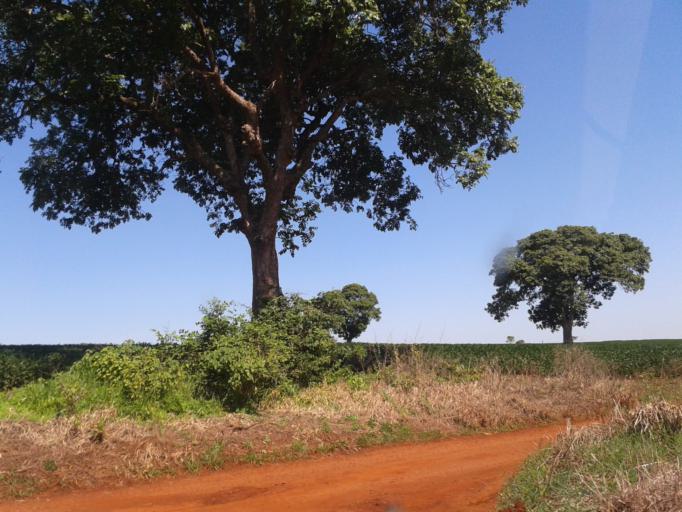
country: BR
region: Minas Gerais
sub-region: Centralina
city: Centralina
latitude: -18.6516
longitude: -49.2992
